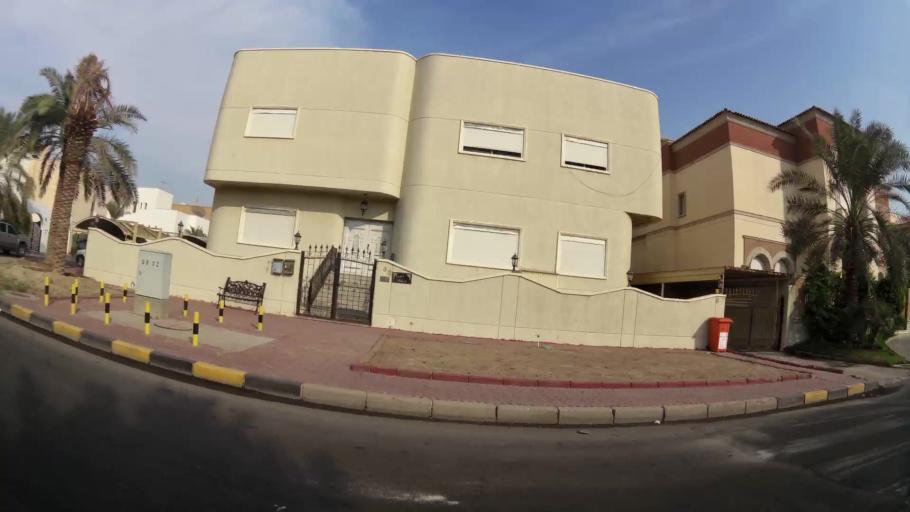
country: KW
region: Al Farwaniyah
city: Janub as Surrah
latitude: 29.3114
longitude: 47.9888
